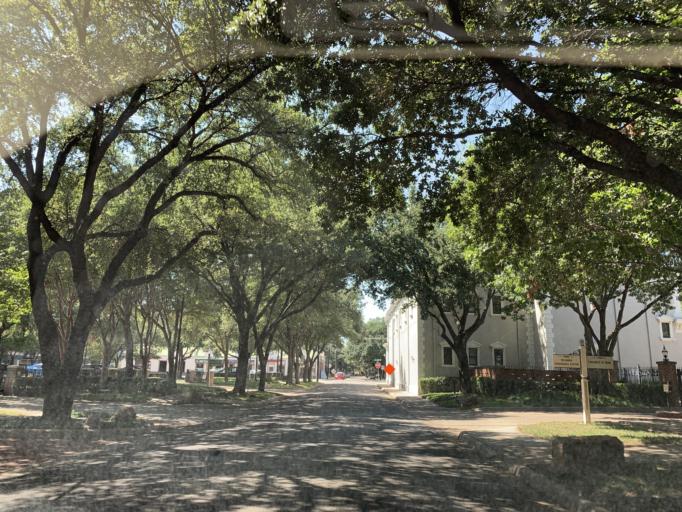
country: US
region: Texas
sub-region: Dallas County
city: Dallas
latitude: 32.7895
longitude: -96.7868
